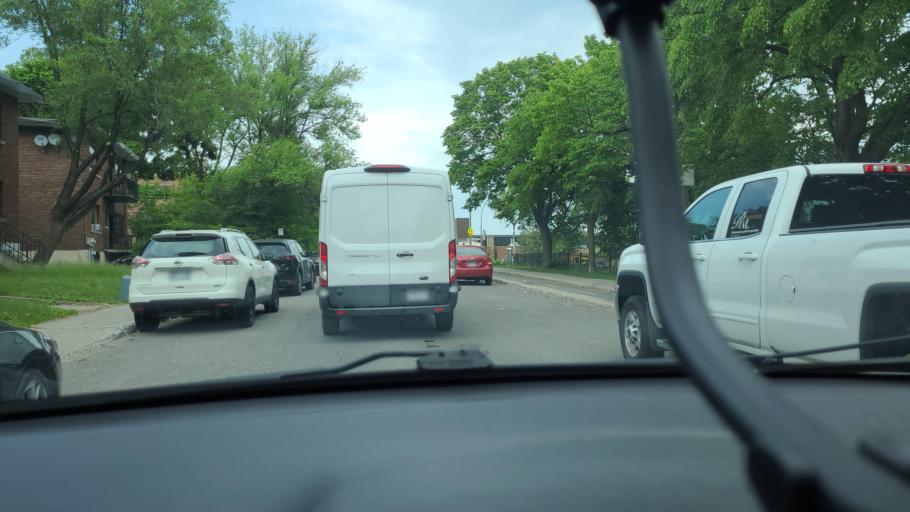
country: CA
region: Quebec
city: Montreal-Ouest
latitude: 45.4555
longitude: -73.6398
